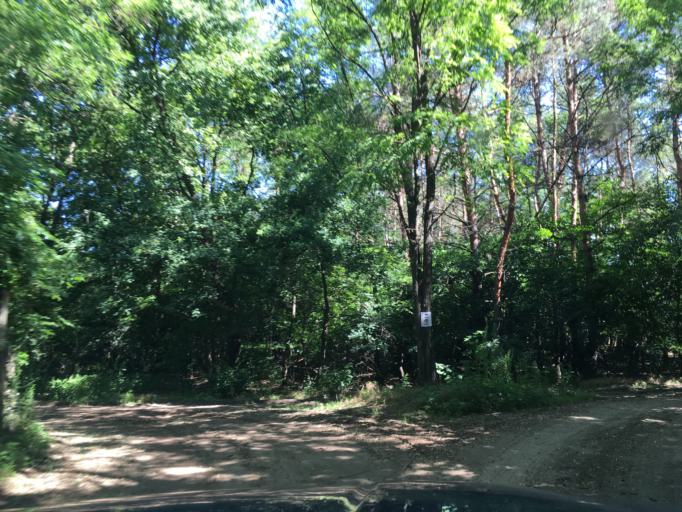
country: HU
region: Hajdu-Bihar
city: Hajdusamson
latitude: 47.5455
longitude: 21.7903
